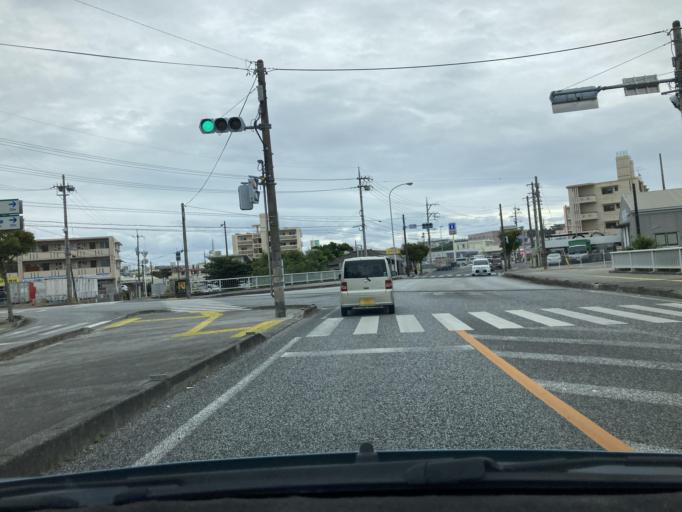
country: JP
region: Okinawa
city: Tomigusuku
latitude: 26.1792
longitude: 127.7178
